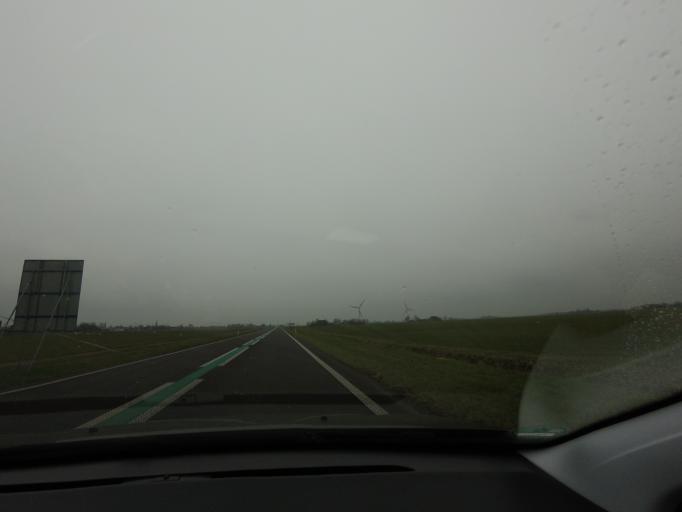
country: NL
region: Friesland
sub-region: Gemeente Littenseradiel
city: Wommels
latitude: 53.1194
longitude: 5.5890
